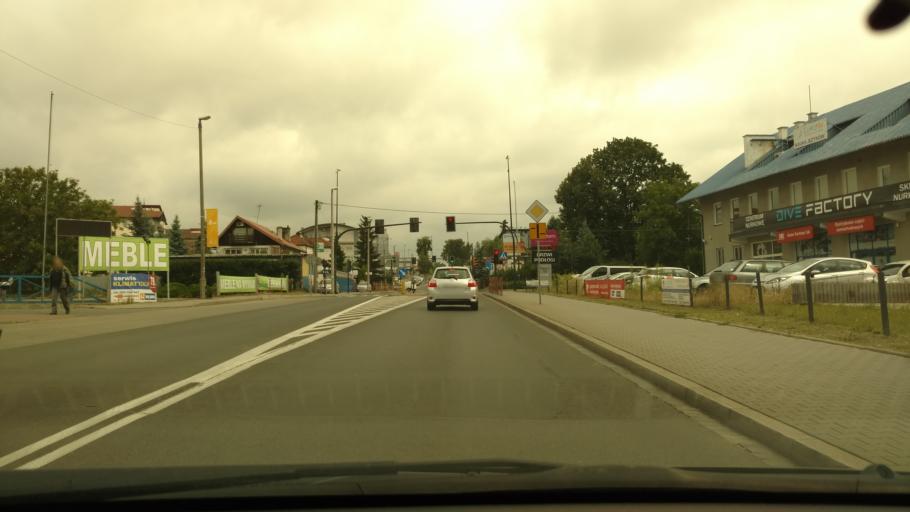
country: PL
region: Lesser Poland Voivodeship
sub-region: Krakow
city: Krakow
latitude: 50.0967
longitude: 19.9619
